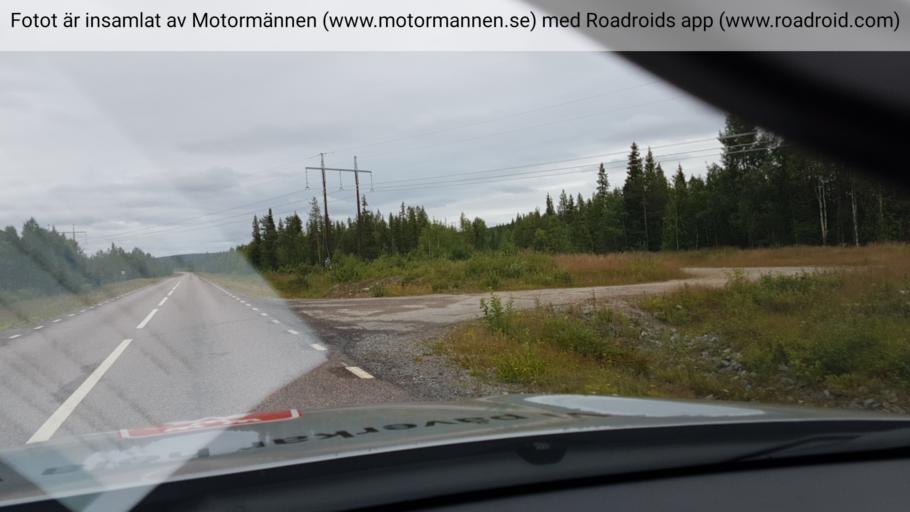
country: SE
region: Norrbotten
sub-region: Gallivare Kommun
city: Gaellivare
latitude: 67.0735
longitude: 21.4643
